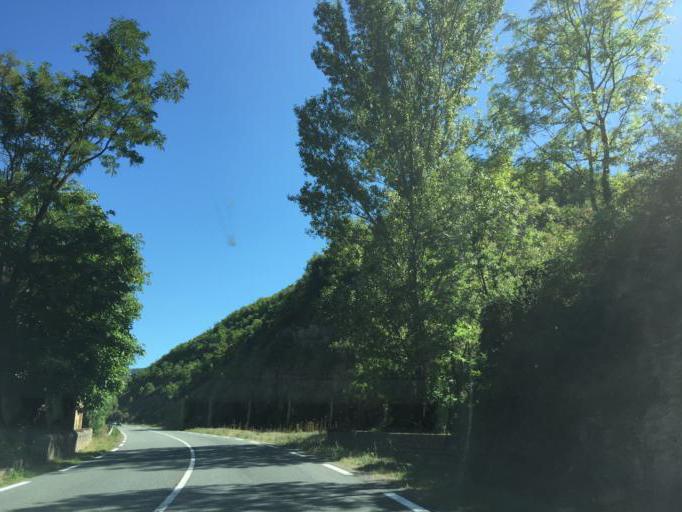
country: FR
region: Midi-Pyrenees
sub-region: Departement de l'Aveyron
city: Saint-Georges-de-Luzencon
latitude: 44.0037
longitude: 2.9648
